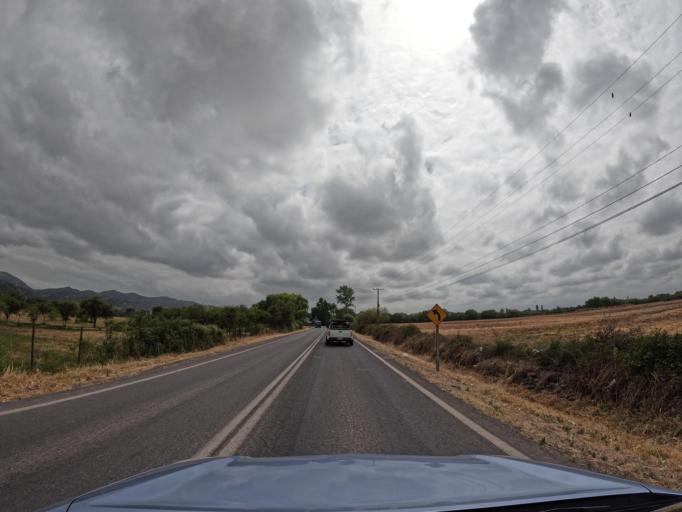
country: CL
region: Maule
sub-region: Provincia de Curico
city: Teno
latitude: -34.8463
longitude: -71.1877
